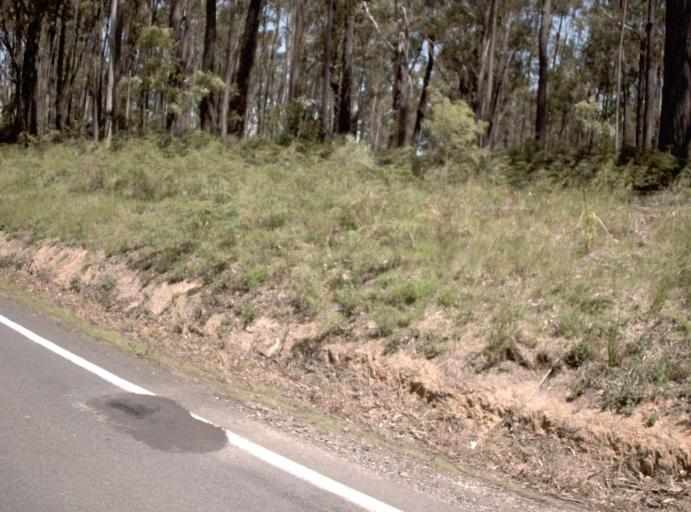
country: AU
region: New South Wales
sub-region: Bombala
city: Bombala
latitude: -37.5877
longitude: 148.9549
